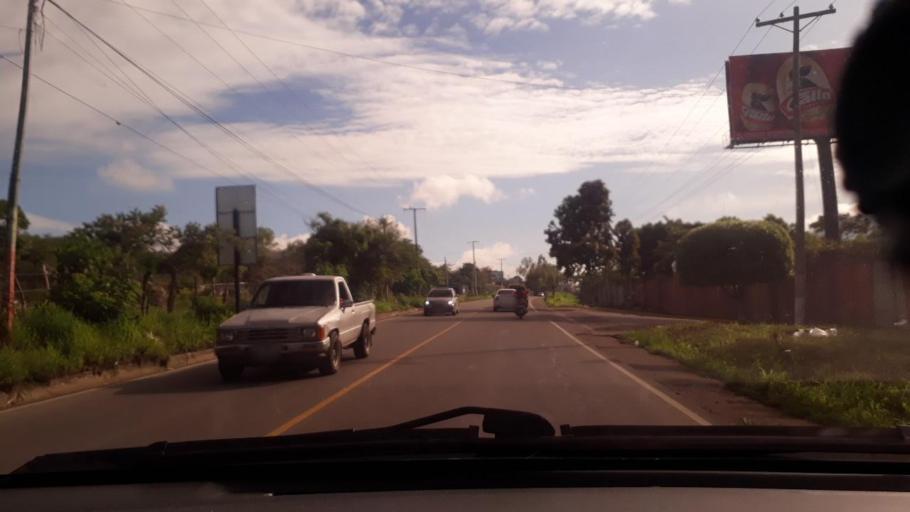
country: GT
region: Jutiapa
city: El Progreso
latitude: 14.3374
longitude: -89.8550
